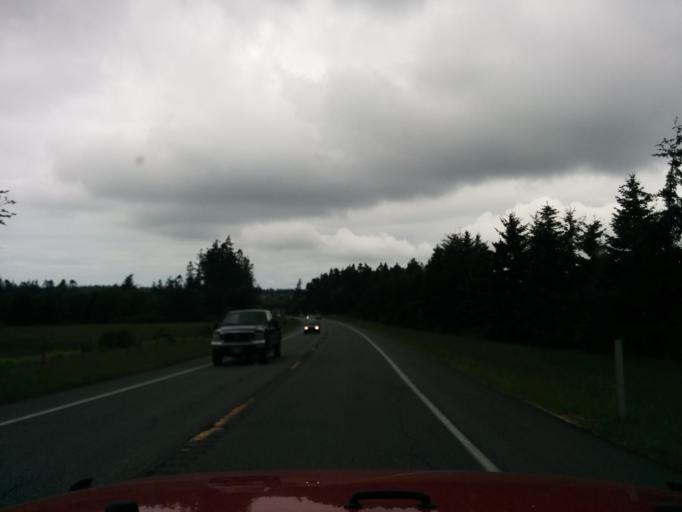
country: US
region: Washington
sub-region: Island County
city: Coupeville
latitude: 48.2103
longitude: -122.6717
